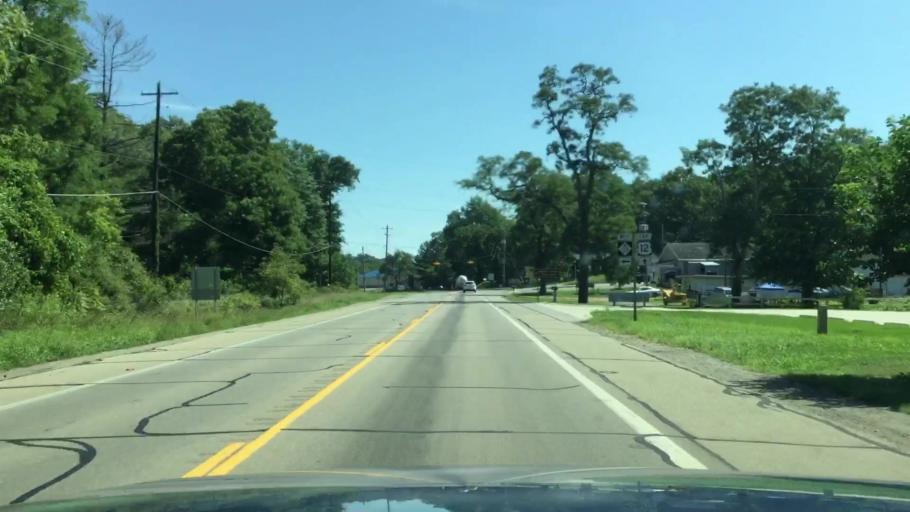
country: US
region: Michigan
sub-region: Jackson County
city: Brooklyn
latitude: 42.0566
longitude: -84.1424
